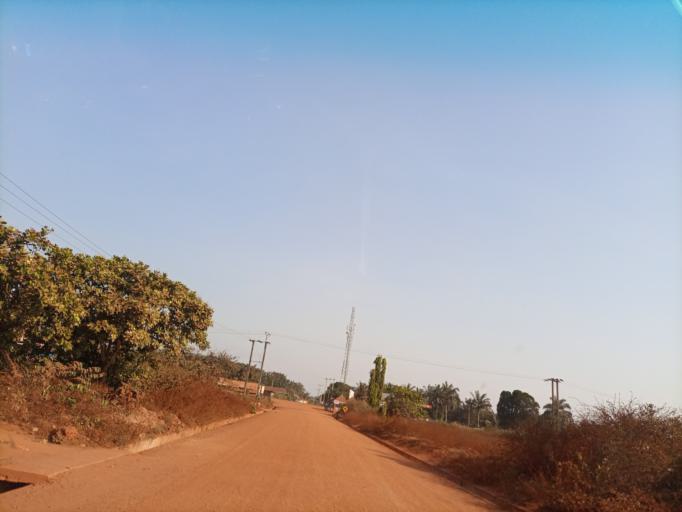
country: NG
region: Enugu
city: Opi
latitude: 6.7472
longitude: 7.4117
